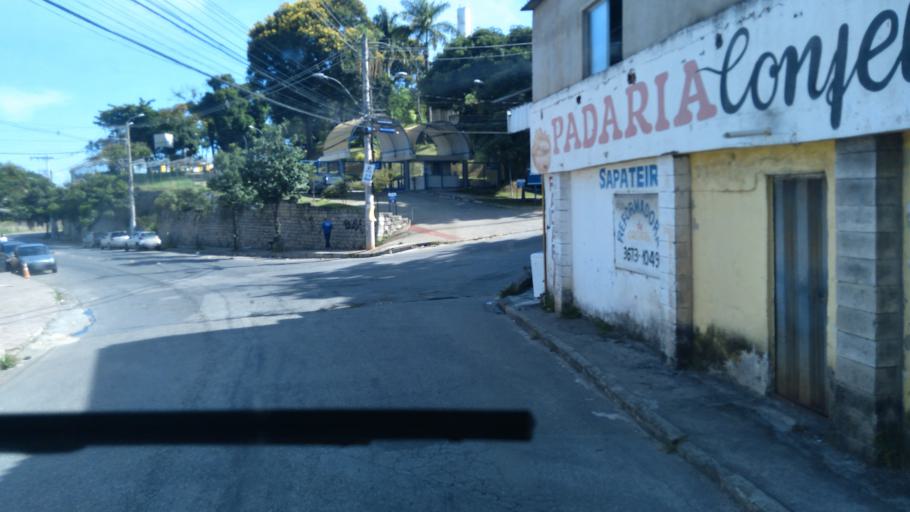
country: BR
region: Minas Gerais
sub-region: Santa Luzia
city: Santa Luzia
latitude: -19.8494
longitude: -43.8855
